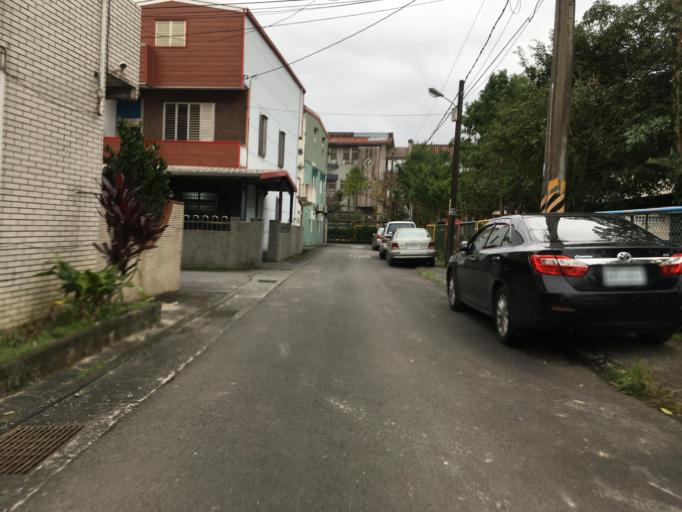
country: TW
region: Taiwan
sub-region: Yilan
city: Yilan
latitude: 24.6310
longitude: 121.7919
